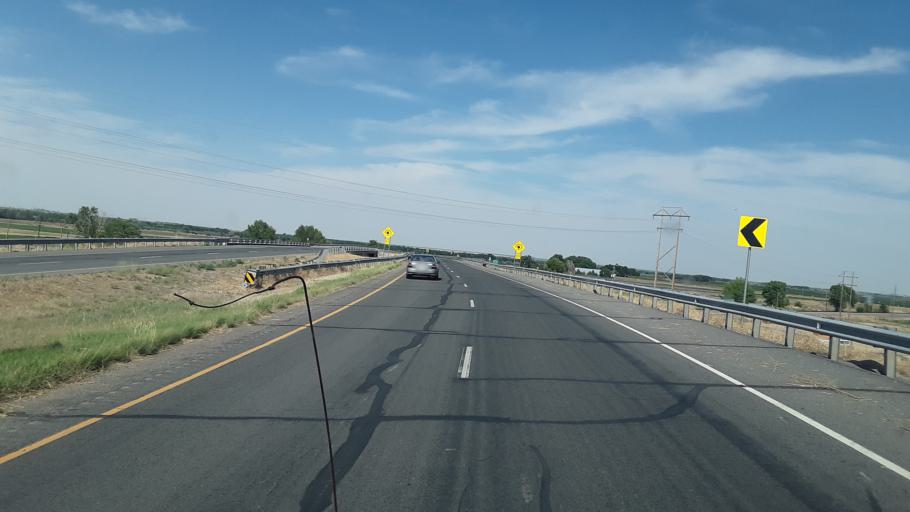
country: US
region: Colorado
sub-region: Otero County
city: Rocky Ford
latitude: 38.1022
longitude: -103.8451
